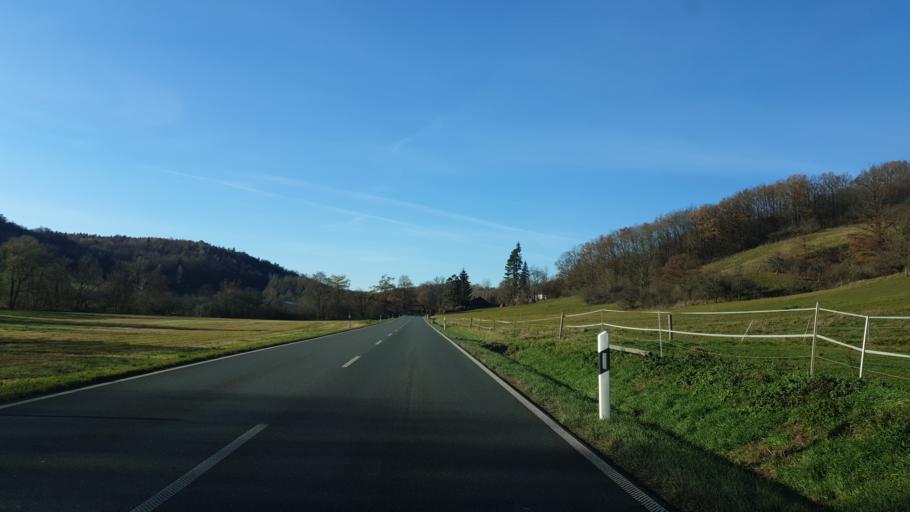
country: DE
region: Thuringia
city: Rauda
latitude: 50.9526
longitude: 11.9360
